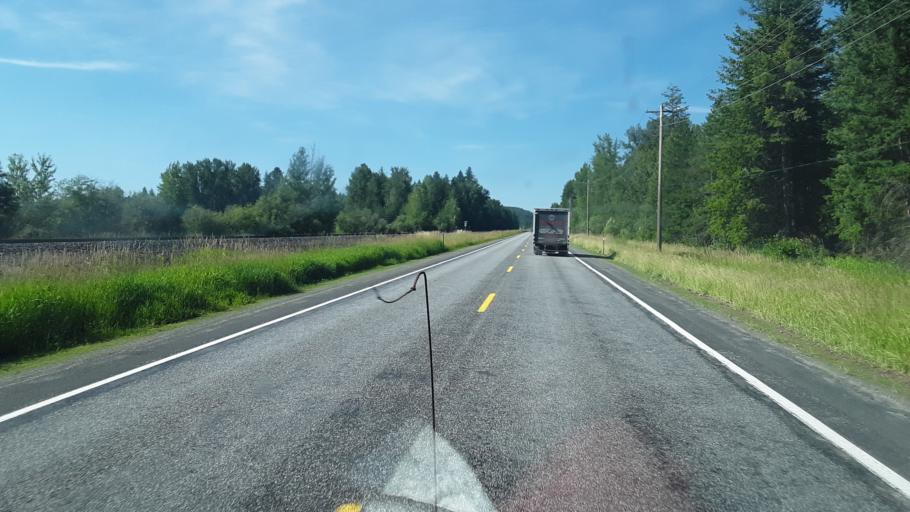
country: US
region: Idaho
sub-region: Bonner County
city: Ponderay
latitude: 48.4456
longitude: -116.4827
